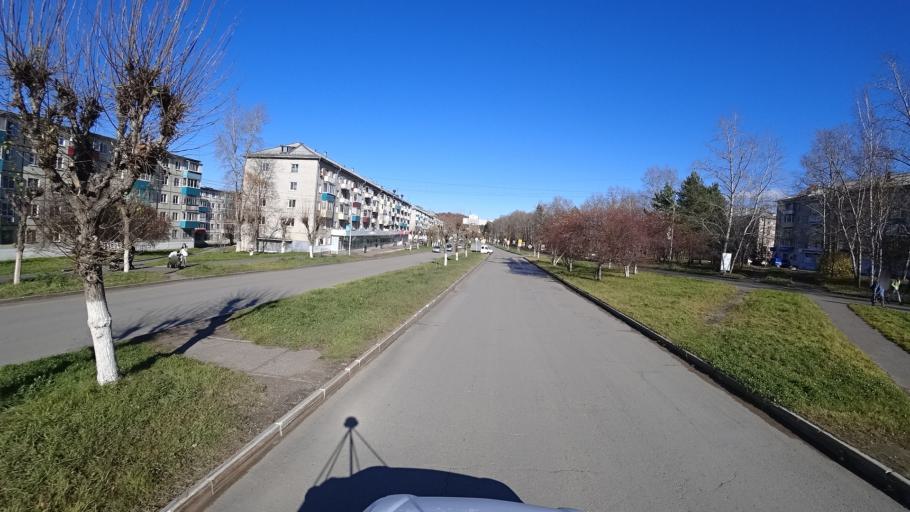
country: RU
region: Khabarovsk Krai
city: Amursk
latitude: 50.2228
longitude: 136.9044
